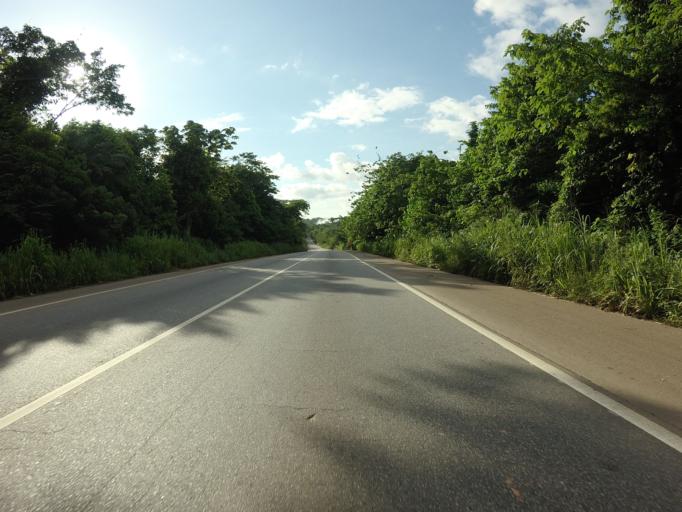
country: GH
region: Ashanti
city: Tafo
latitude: 6.8921
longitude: -1.6493
